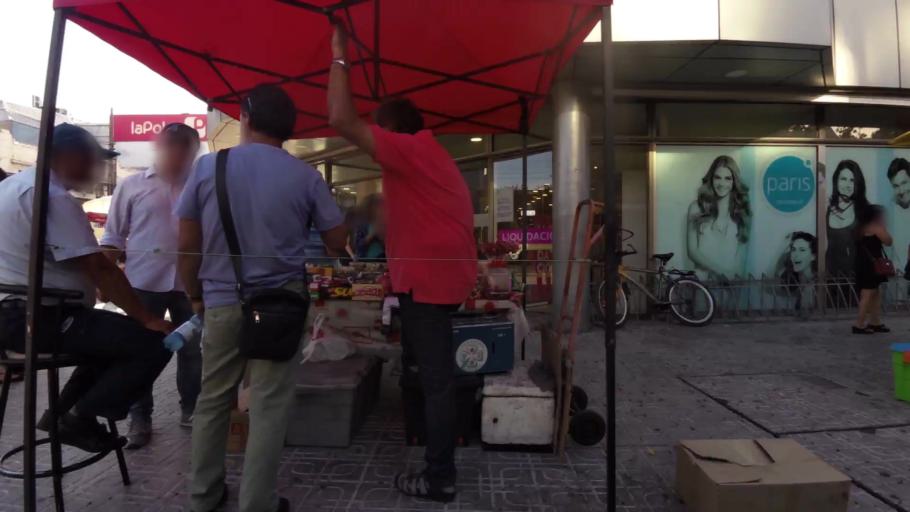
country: CL
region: Maule
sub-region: Provincia de Talca
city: Talca
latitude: -35.4278
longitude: -71.6556
